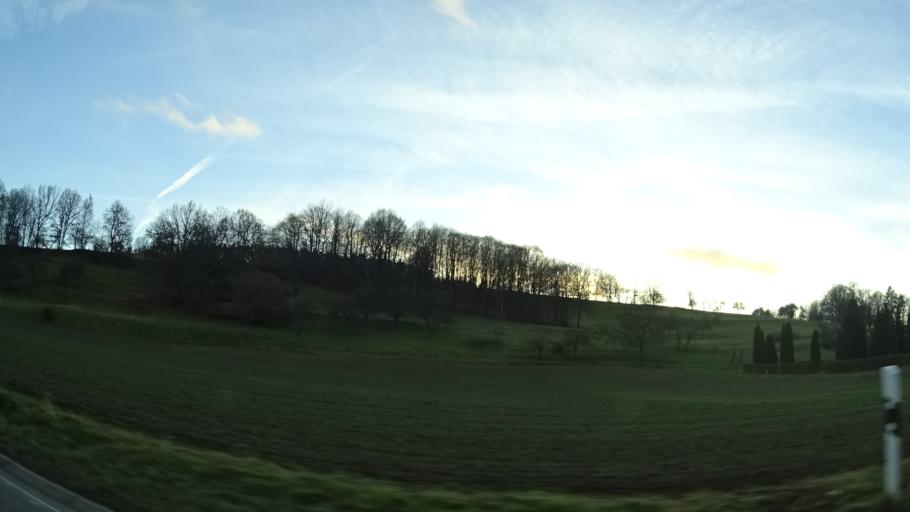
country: DE
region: Thuringia
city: Reinstadt
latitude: 50.7690
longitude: 11.4643
